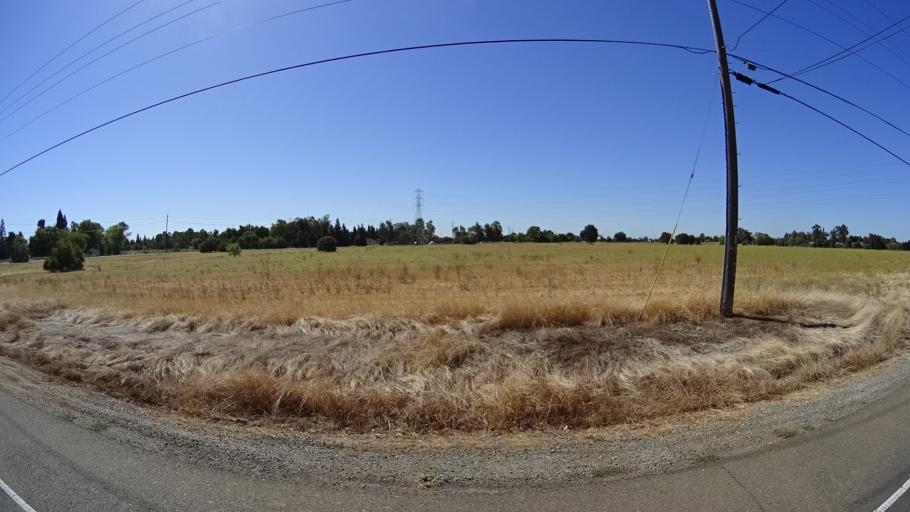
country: US
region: California
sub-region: Sacramento County
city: Wilton
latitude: 38.4236
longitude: -121.3115
